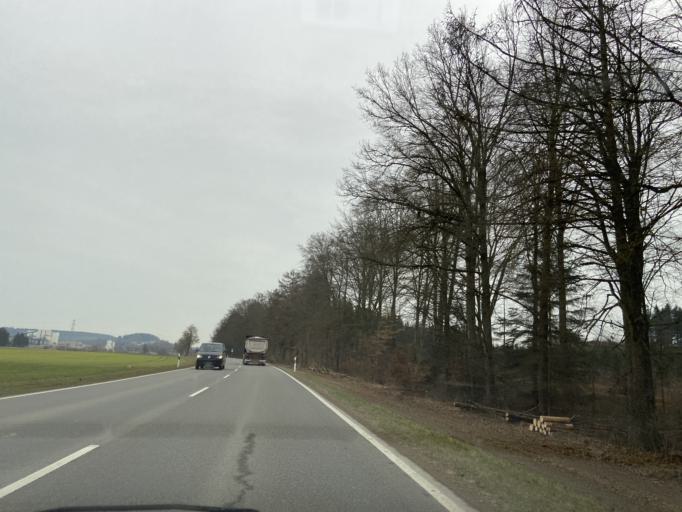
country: DE
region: Baden-Wuerttemberg
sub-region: Tuebingen Region
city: Ostrach
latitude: 47.9642
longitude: 9.3651
